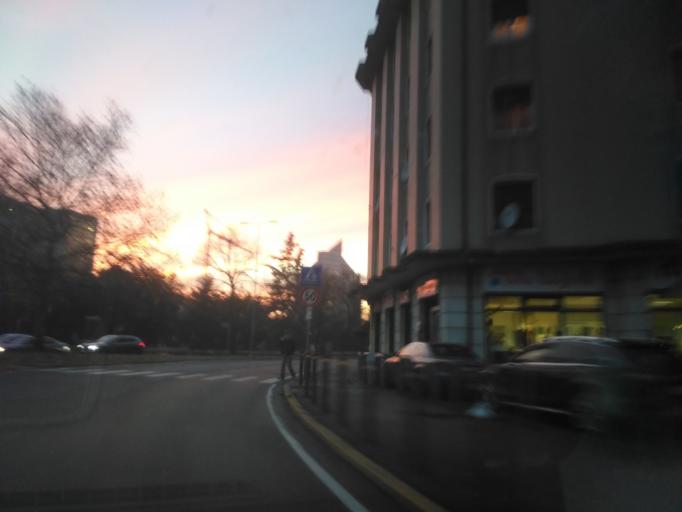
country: IT
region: Lombardy
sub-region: Provincia di Brescia
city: Brescia
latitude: 45.5584
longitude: 10.2270
